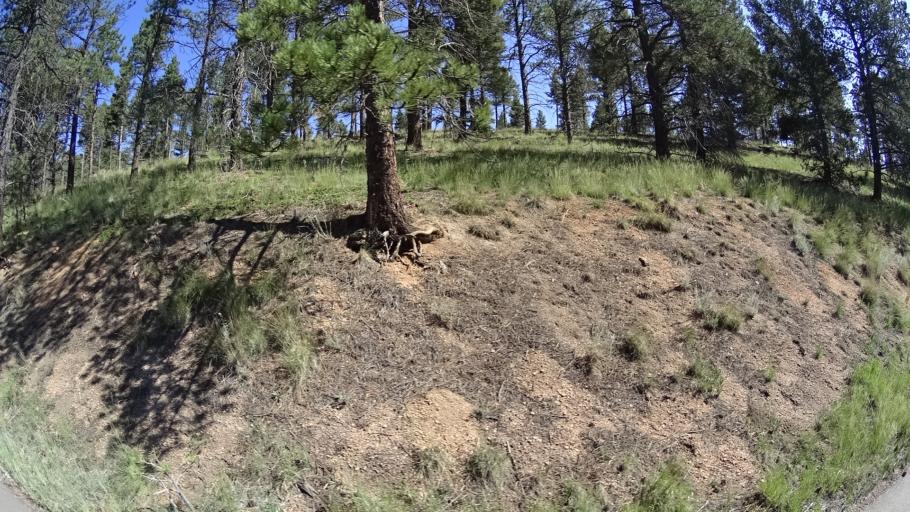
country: US
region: Colorado
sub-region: El Paso County
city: Cascade-Chipita Park
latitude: 38.9119
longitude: -105.0272
